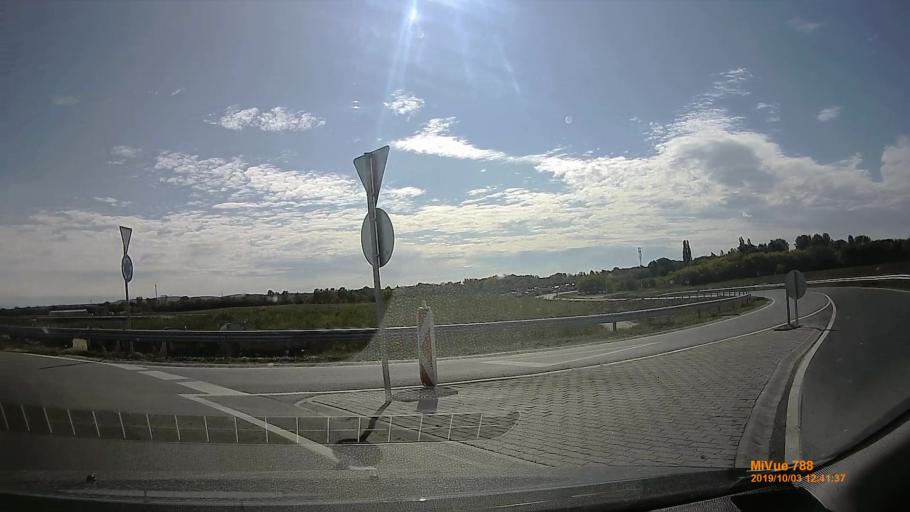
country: HU
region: Pest
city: Szodliget
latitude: 47.7329
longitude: 19.1593
